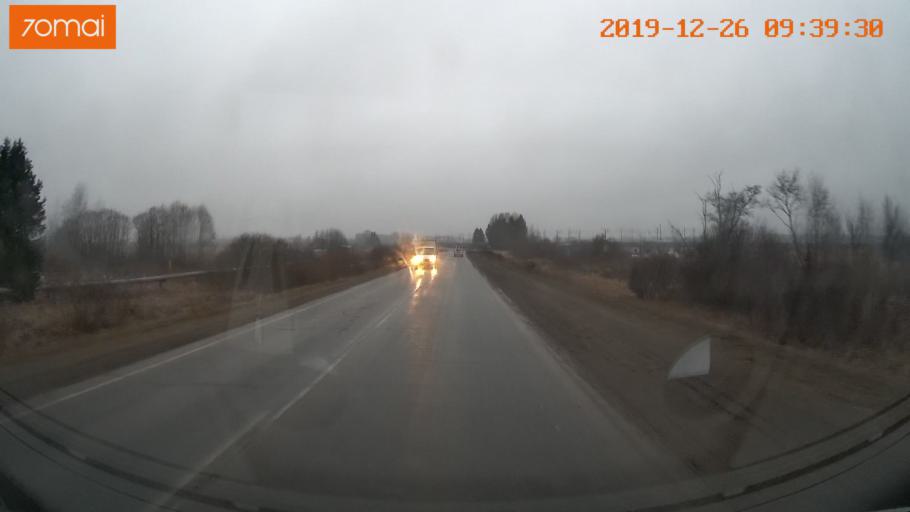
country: RU
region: Vologda
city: Vologda
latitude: 59.1552
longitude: 40.0243
